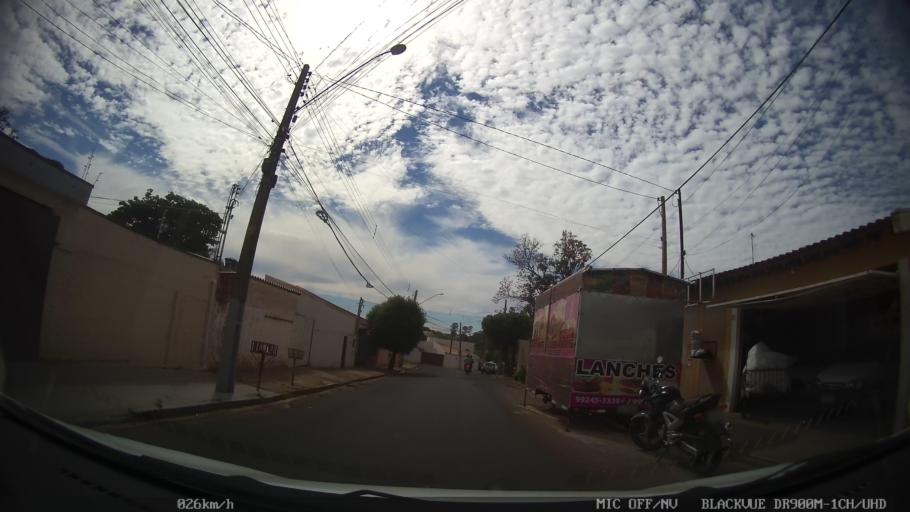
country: BR
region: Sao Paulo
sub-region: Catanduva
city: Catanduva
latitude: -21.1567
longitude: -48.9738
